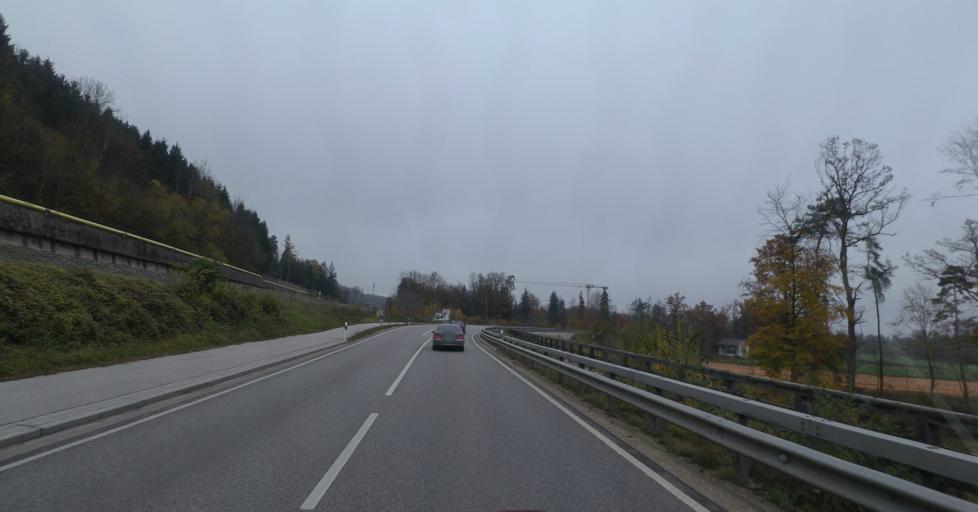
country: DE
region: Bavaria
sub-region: Upper Bavaria
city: Engelsberg
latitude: 48.1148
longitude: 12.5709
